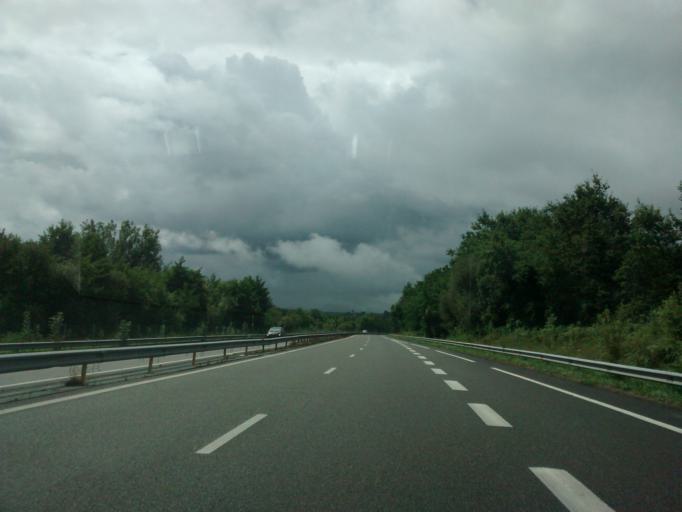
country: FR
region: Aquitaine
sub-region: Departement des Pyrenees-Atlantiques
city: Urt
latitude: 43.4630
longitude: -1.2893
